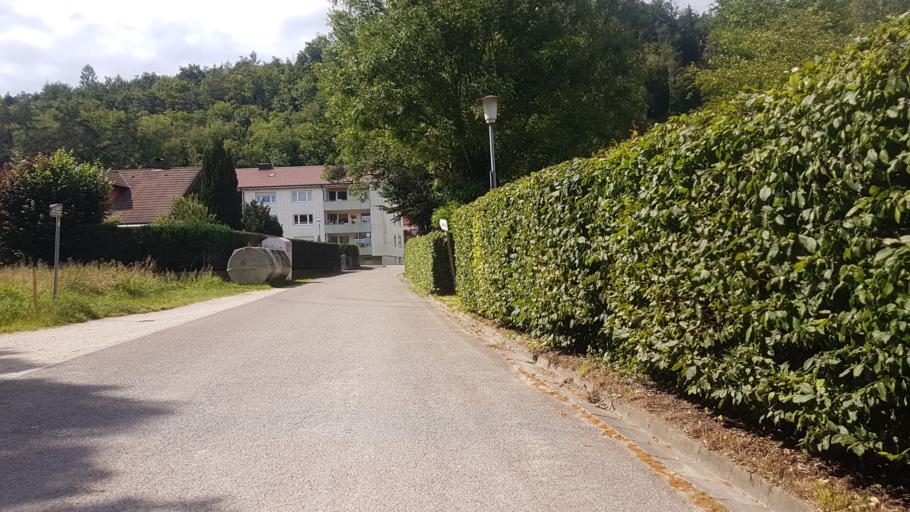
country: DE
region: Bavaria
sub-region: Regierungsbezirk Mittelfranken
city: Pappenheim
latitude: 48.9346
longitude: 10.9695
